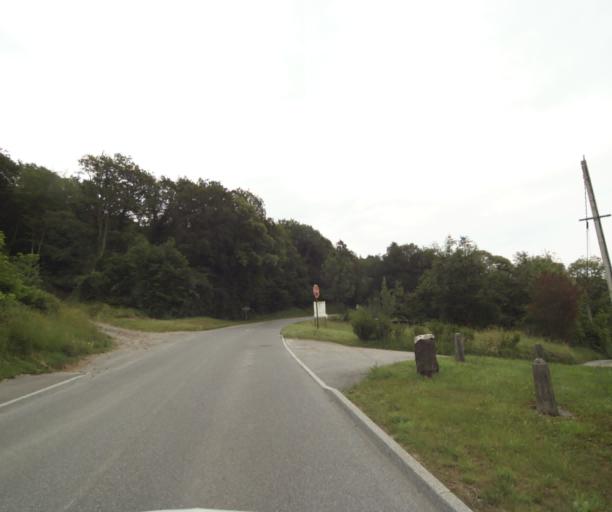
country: FR
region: Rhone-Alpes
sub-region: Departement de la Haute-Savoie
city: Thonon-les-Bains
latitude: 46.3502
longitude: 6.4790
